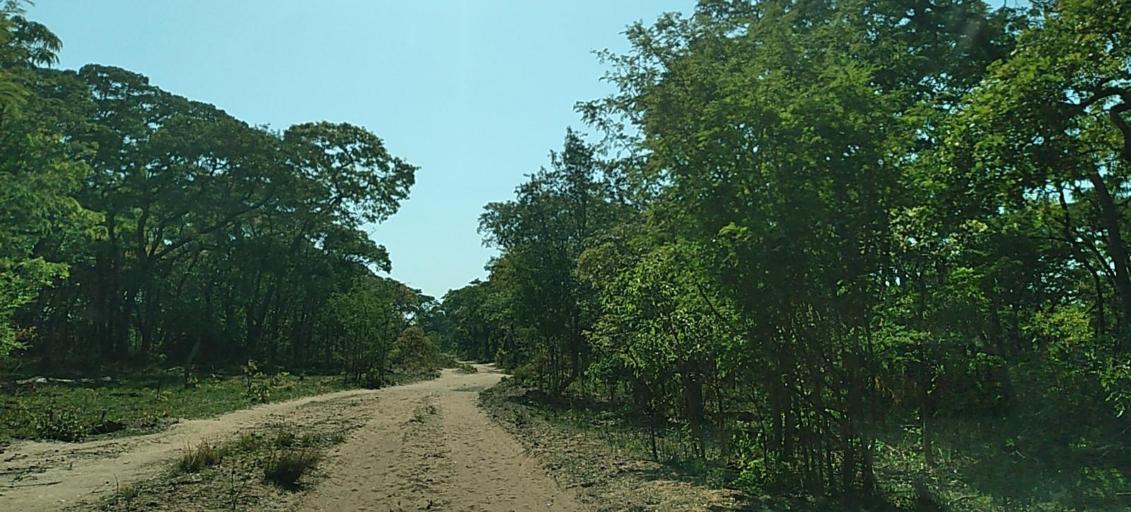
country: ZM
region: Central
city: Mkushi
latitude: -13.4701
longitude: 28.9706
